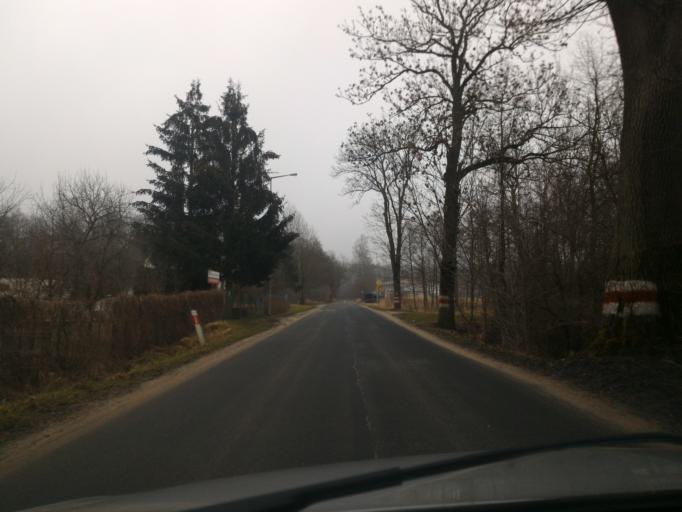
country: PL
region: Lower Silesian Voivodeship
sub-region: Powiat zgorzelecki
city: Bogatynia
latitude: 50.9080
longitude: 14.9921
